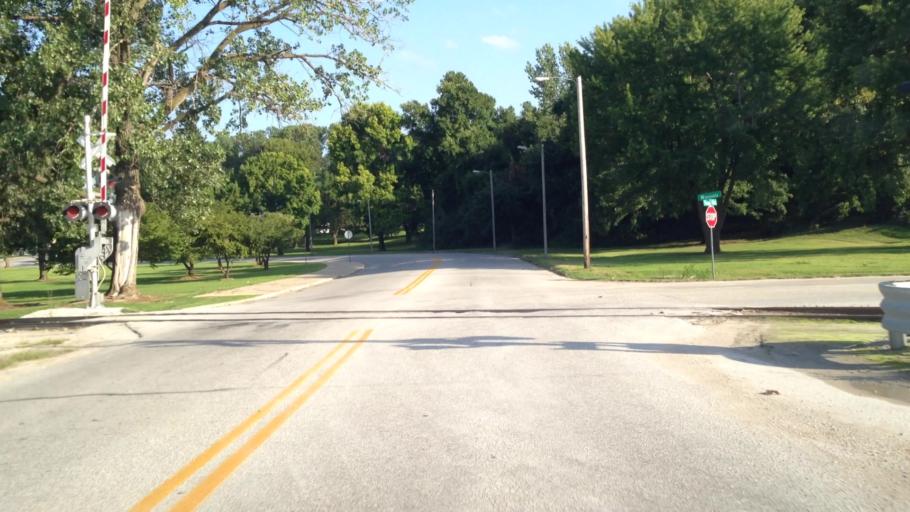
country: US
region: Missouri
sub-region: Jasper County
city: Joplin
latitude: 37.0856
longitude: -94.5054
